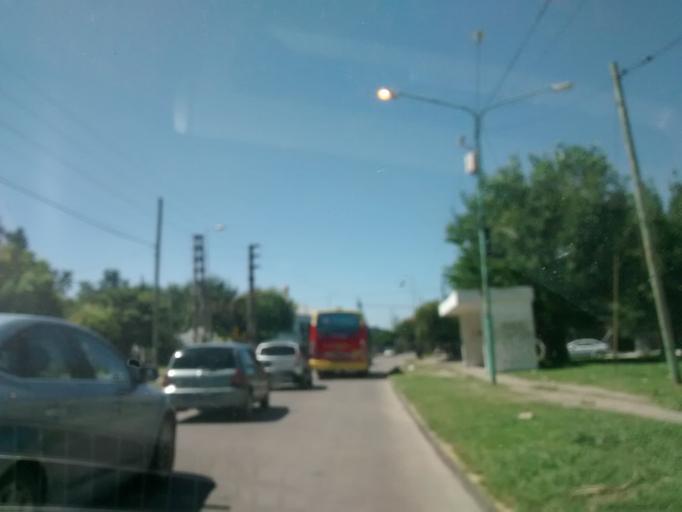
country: AR
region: Buenos Aires
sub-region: Partido de Berisso
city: Berisso
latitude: -34.8776
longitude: -57.8533
